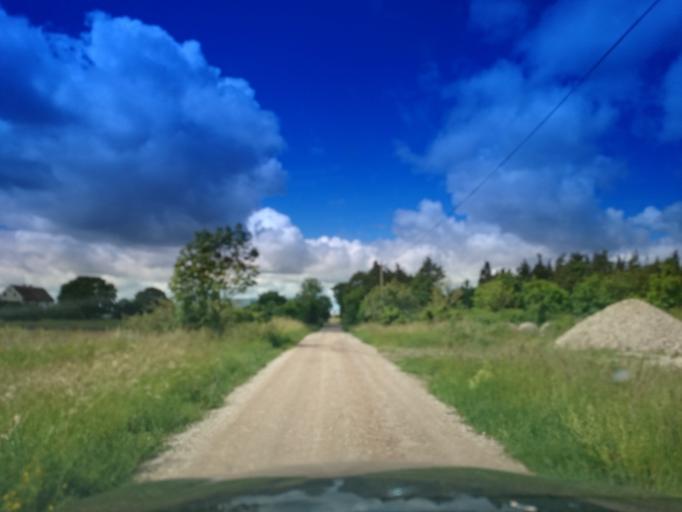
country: SE
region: Gotland
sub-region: Gotland
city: Hemse
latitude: 57.3386
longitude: 18.6214
